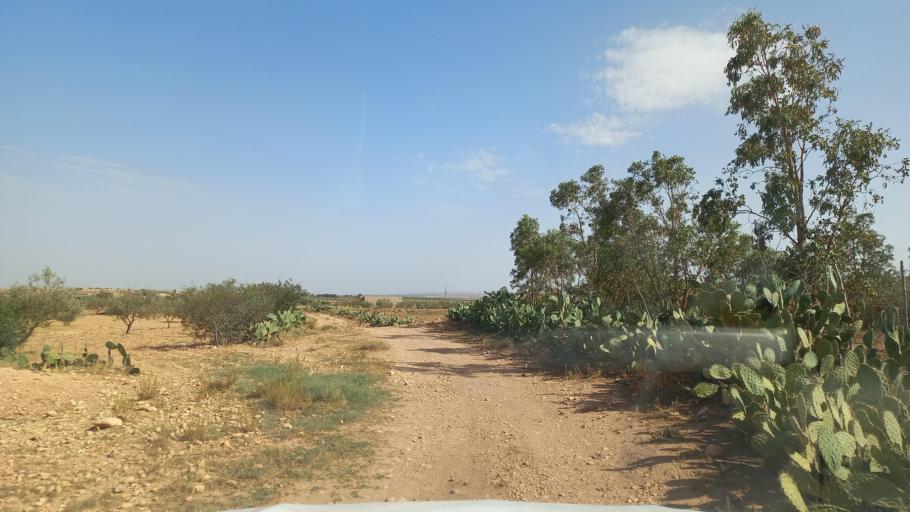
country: TN
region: Al Qasrayn
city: Kasserine
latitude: 35.2812
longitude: 8.9528
